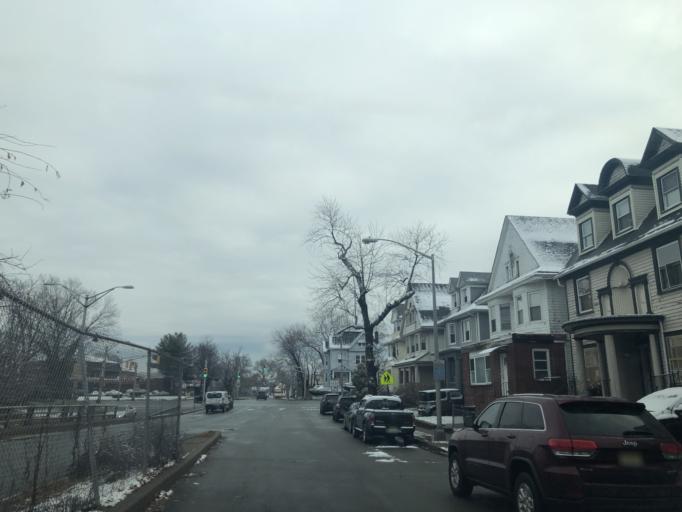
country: US
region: New Jersey
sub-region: Essex County
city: East Orange
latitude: 40.7547
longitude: -74.2058
